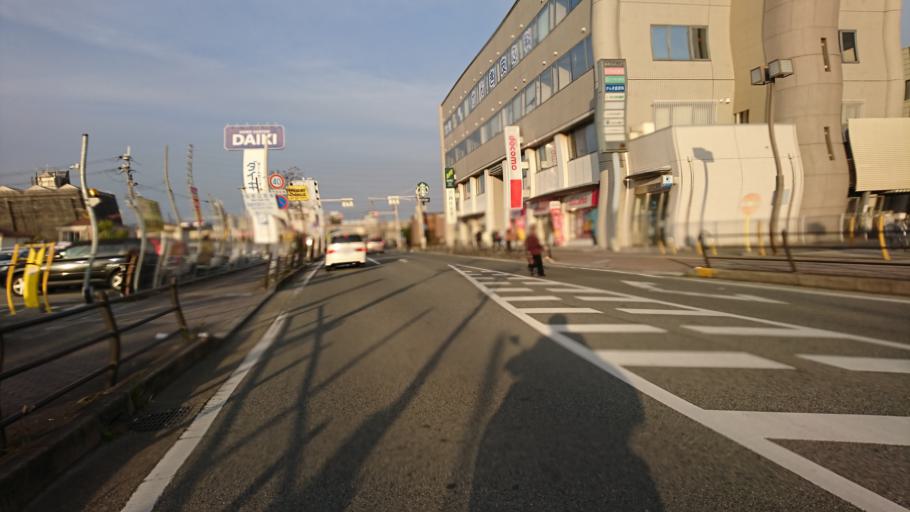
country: JP
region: Hyogo
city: Kakogawacho-honmachi
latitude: 34.7292
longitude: 134.8492
